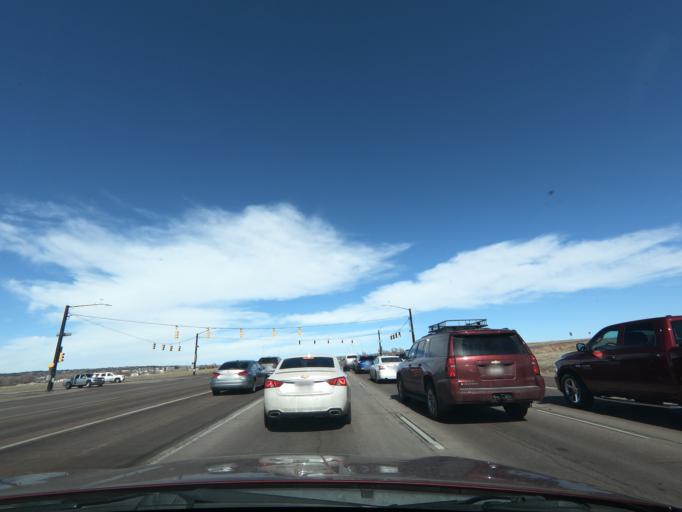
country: US
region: Colorado
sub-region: El Paso County
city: Cimarron Hills
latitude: 38.8241
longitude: -104.7251
